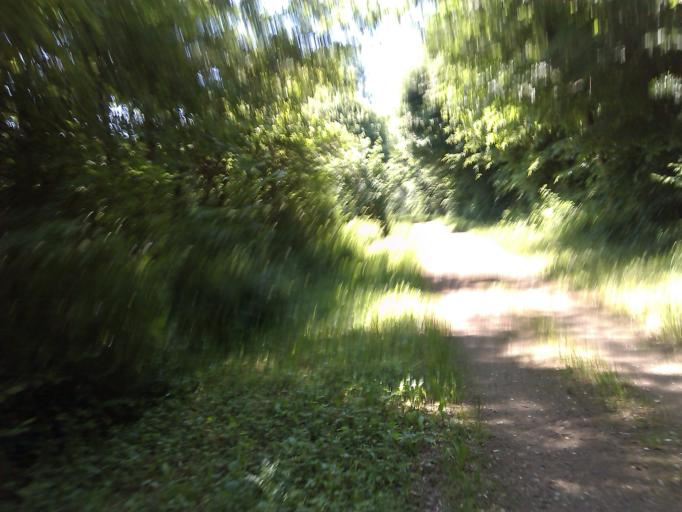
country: FR
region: Centre
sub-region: Departement de l'Indre
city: Saint-Gaultier
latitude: 46.6397
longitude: 1.3817
